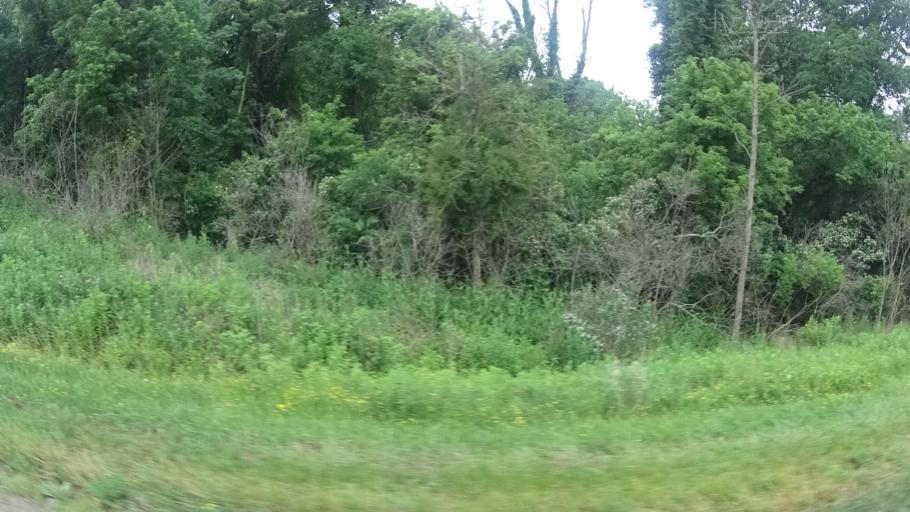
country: US
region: Ohio
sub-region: Erie County
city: Milan
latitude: 41.3368
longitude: -82.5766
